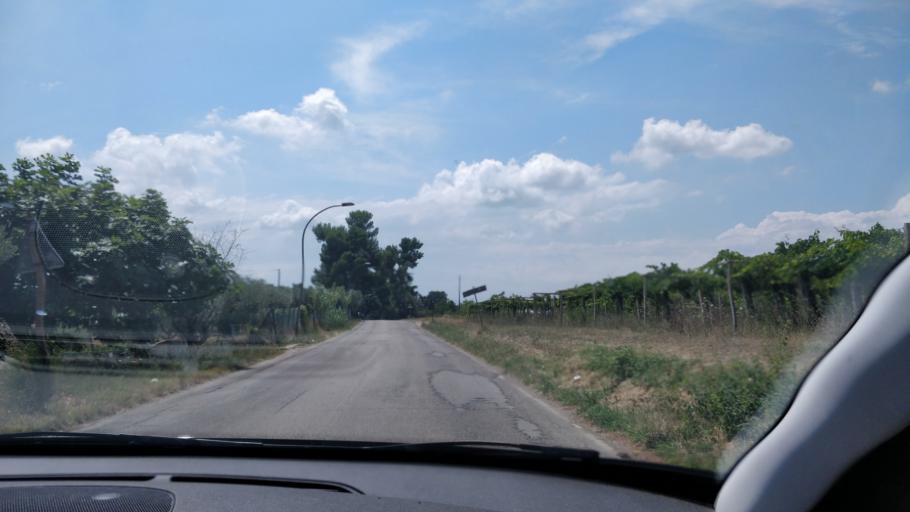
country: IT
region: Abruzzo
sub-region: Provincia di Chieti
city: Torrevecchia
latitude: 42.4144
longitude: 14.2281
